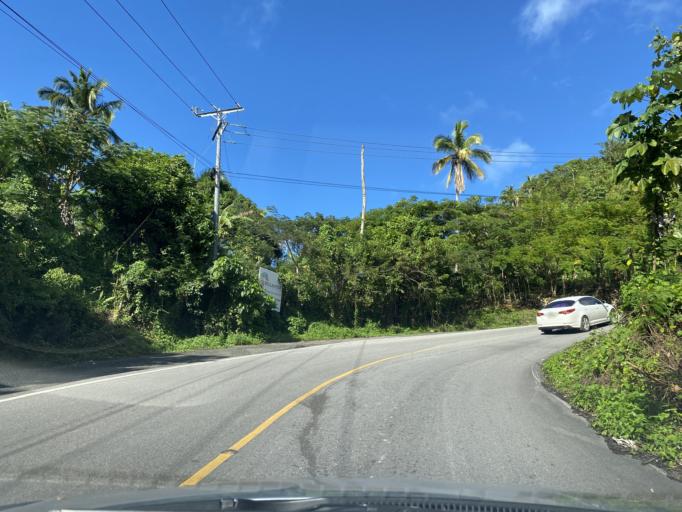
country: DO
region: Samana
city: Sanchez
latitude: 19.2416
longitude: -69.5966
